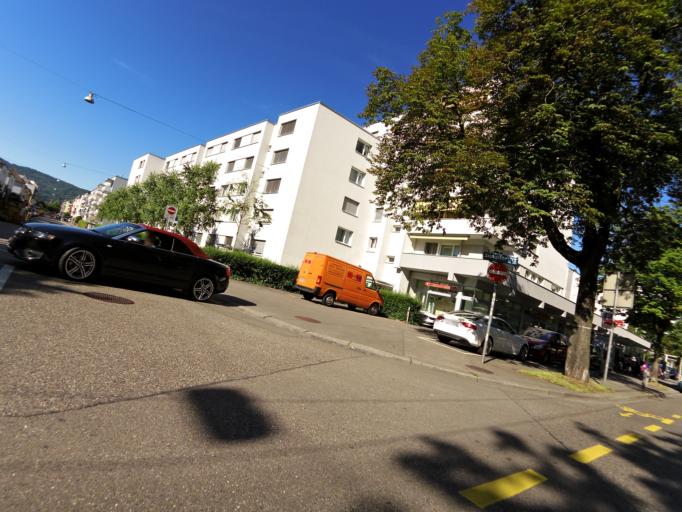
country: CH
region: Zurich
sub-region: Bezirk Zuerich
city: Zuerich (Kreis 9) / Altstetten
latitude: 47.3907
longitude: 8.4897
